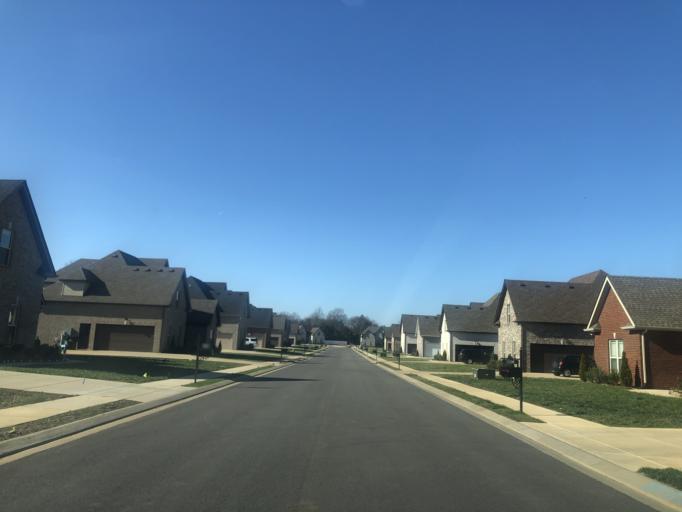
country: US
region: Tennessee
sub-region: Rutherford County
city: Smyrna
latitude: 35.8969
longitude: -86.4805
